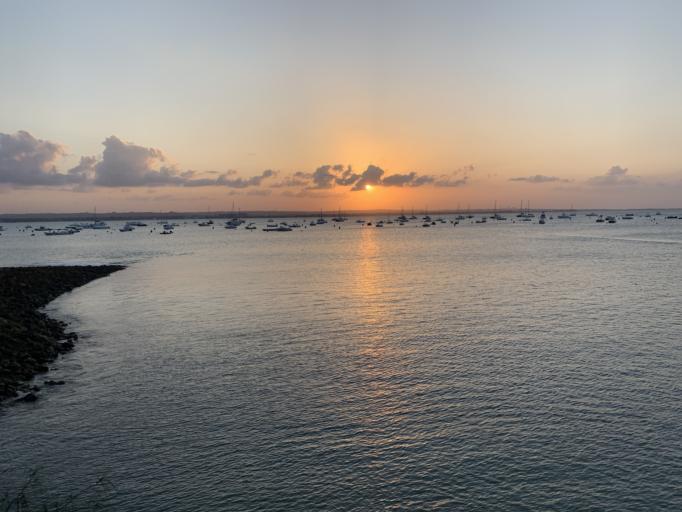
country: TZ
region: Dar es Salaam
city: Magomeni
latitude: -6.7442
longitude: 39.2739
